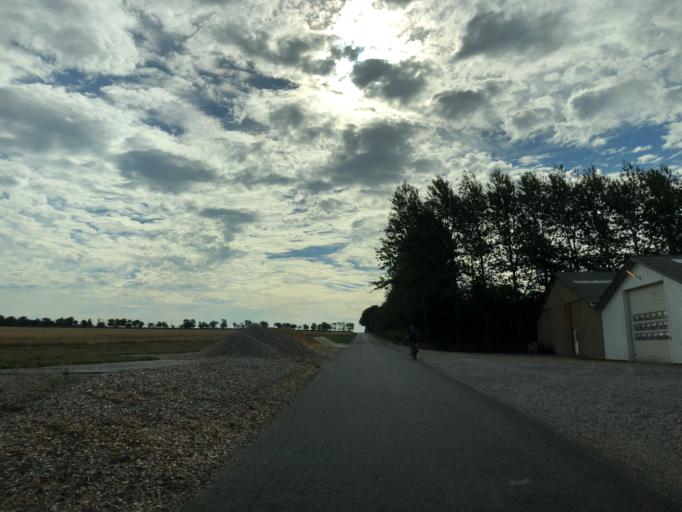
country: DK
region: Central Jutland
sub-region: Ringkobing-Skjern Kommune
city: Skjern
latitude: 56.0435
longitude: 8.4275
